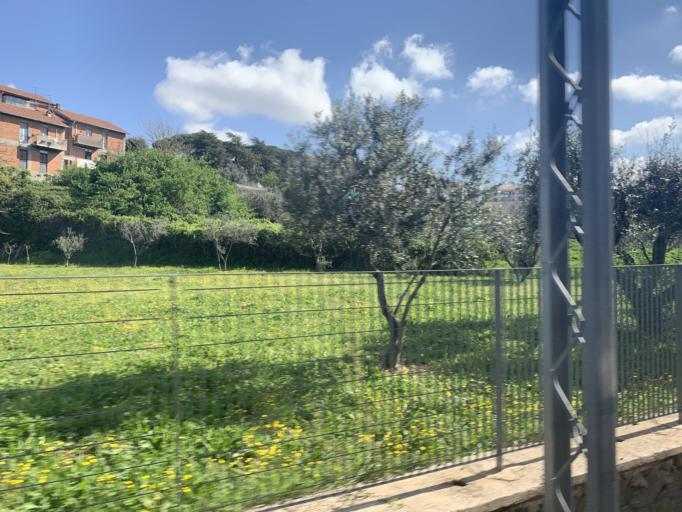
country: IT
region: Latium
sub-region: Citta metropolitana di Roma Capitale
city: Marino
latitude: 41.7705
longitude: 12.6483
